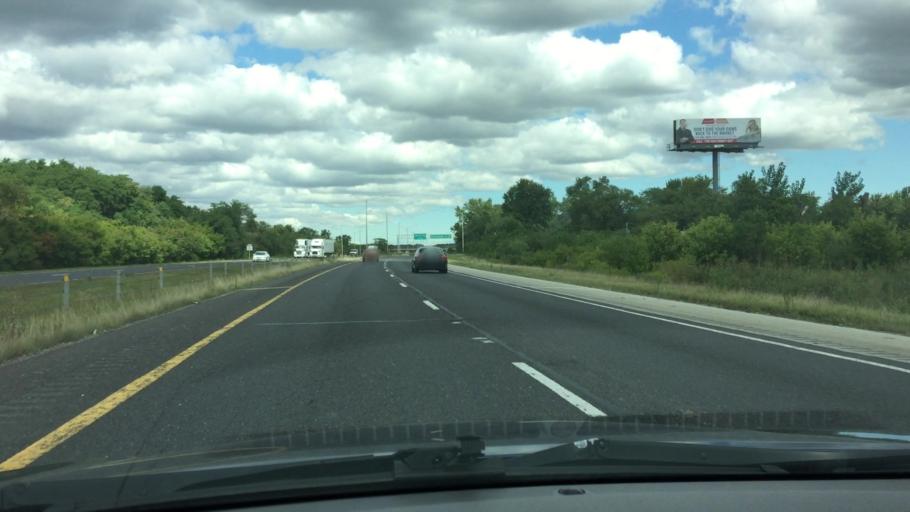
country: US
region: Illinois
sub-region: Cook County
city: Ford Heights
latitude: 41.5263
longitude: -87.5821
